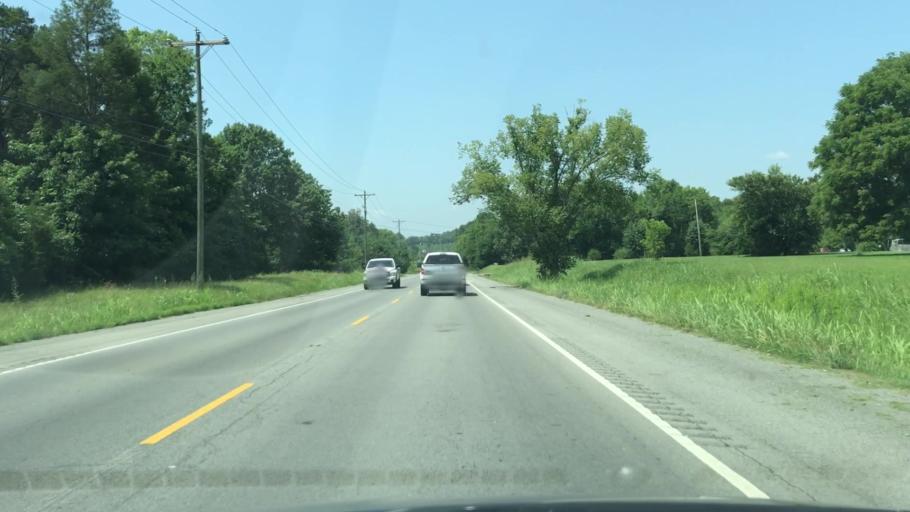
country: US
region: Tennessee
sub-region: Rutherford County
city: La Vergne
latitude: 36.0639
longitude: -86.5917
